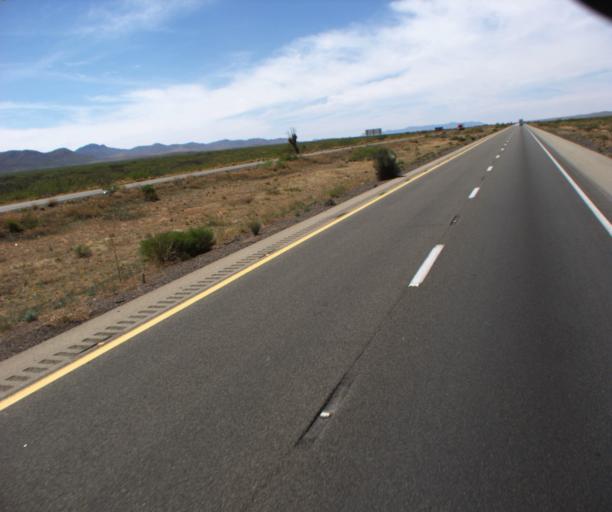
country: US
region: Arizona
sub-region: Cochise County
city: Willcox
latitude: 32.3367
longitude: -109.5410
